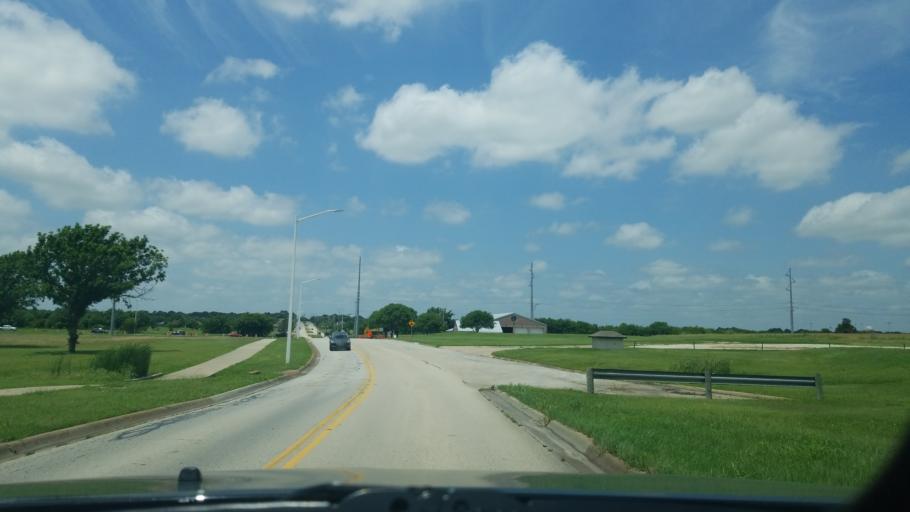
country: US
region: Texas
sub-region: Denton County
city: Denton
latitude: 33.2395
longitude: -97.1579
